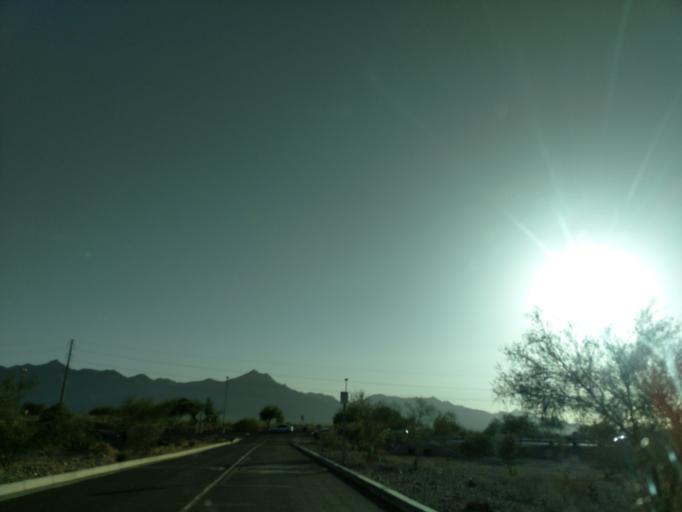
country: US
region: Arizona
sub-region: Maricopa County
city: Laveen
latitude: 33.3117
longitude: -112.1597
